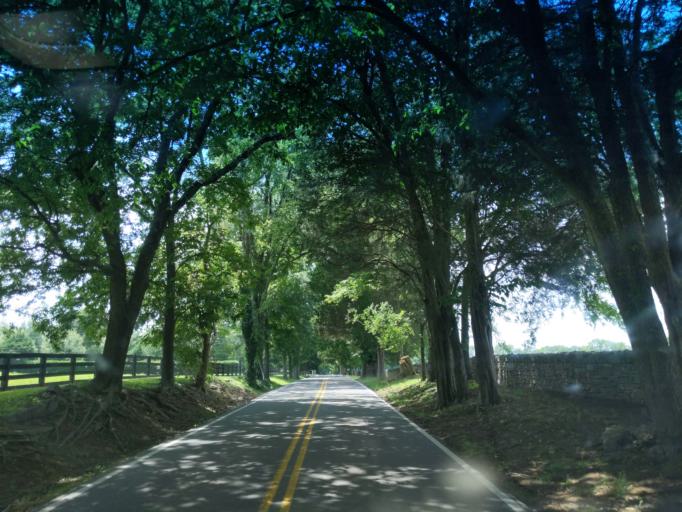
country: US
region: Tennessee
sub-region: Williamson County
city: Brentwood Estates
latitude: 36.0175
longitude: -86.7613
